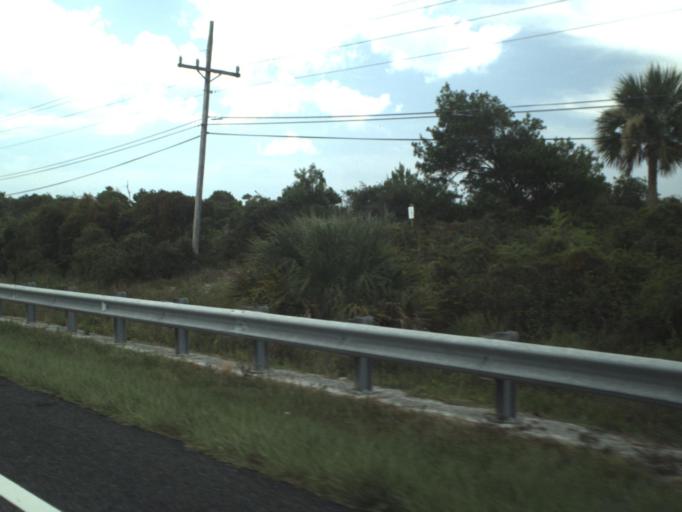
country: US
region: Florida
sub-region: Martin County
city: Hobe Sound
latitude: 27.0181
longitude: -80.1061
